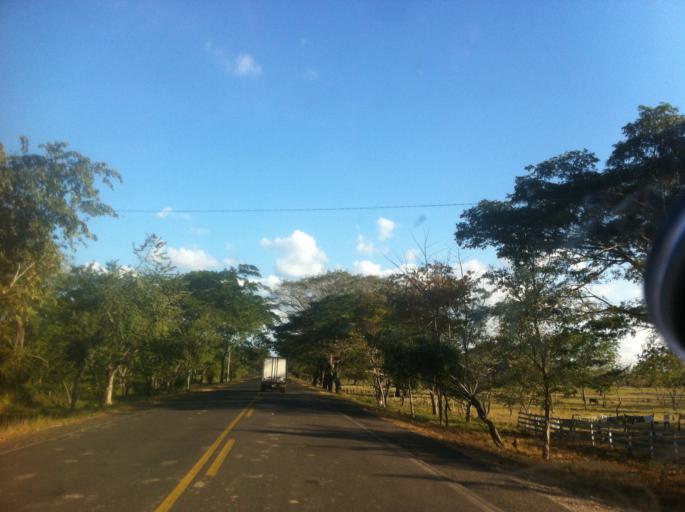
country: NI
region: Rio San Juan
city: Morrito
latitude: 11.6837
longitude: -84.9329
